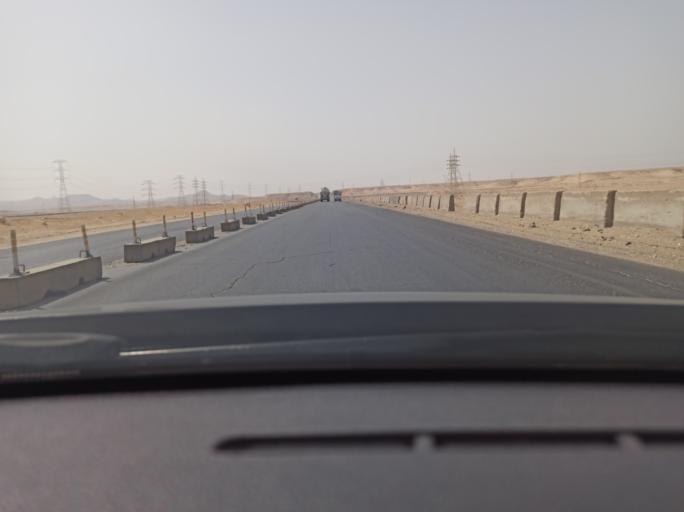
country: EG
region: Muhafazat Bani Suwayf
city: Bush
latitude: 29.1638
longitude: 31.2386
